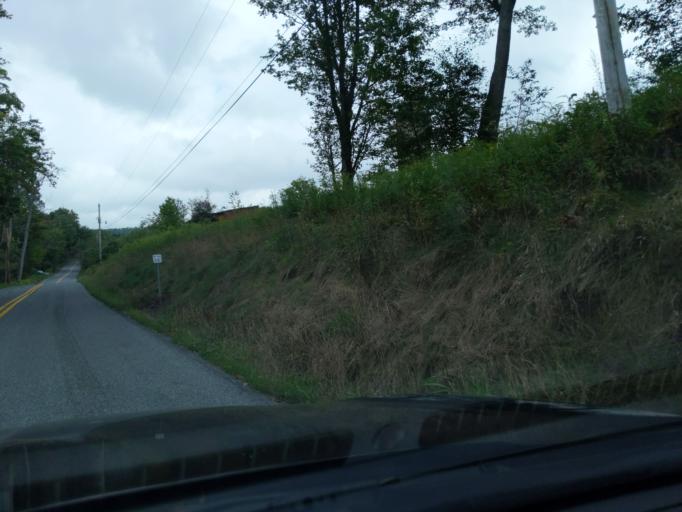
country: US
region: Pennsylvania
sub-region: Cambria County
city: Portage
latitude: 40.3410
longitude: -78.5833
